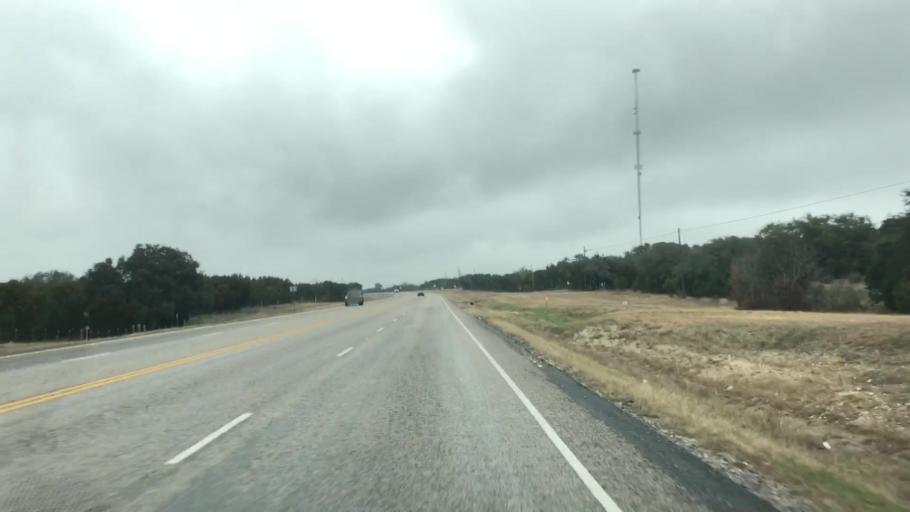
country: US
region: Texas
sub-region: Burnet County
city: Burnet
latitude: 30.8683
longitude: -98.2350
